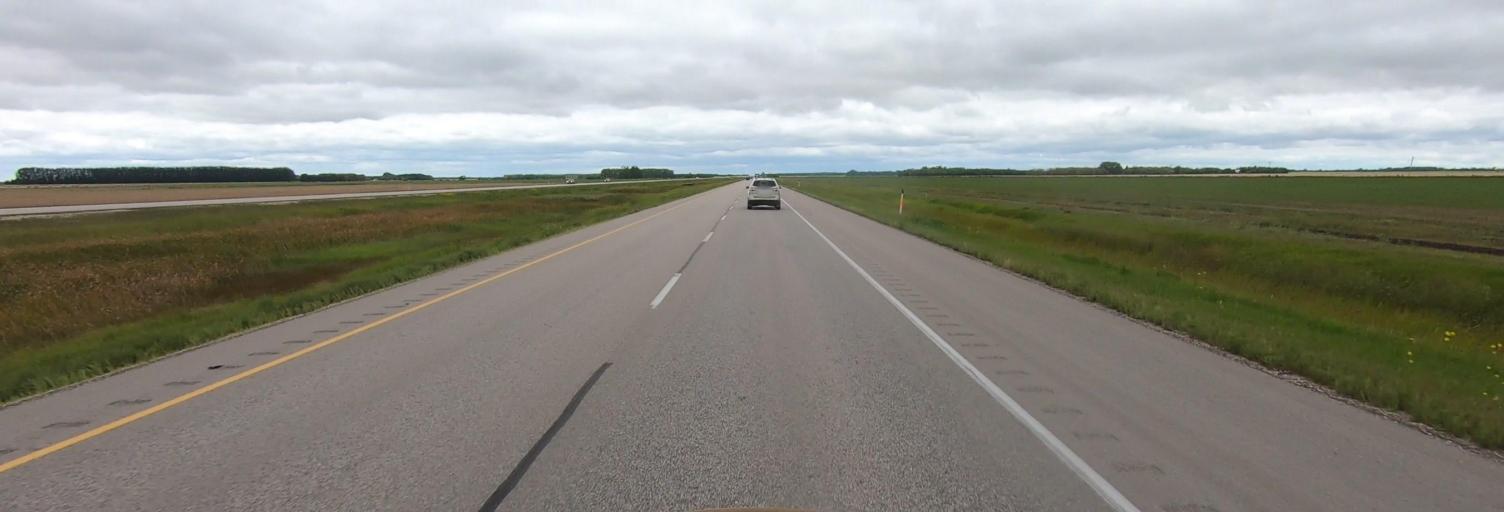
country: CA
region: Manitoba
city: Portage la Prairie
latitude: 49.9416
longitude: -97.9440
